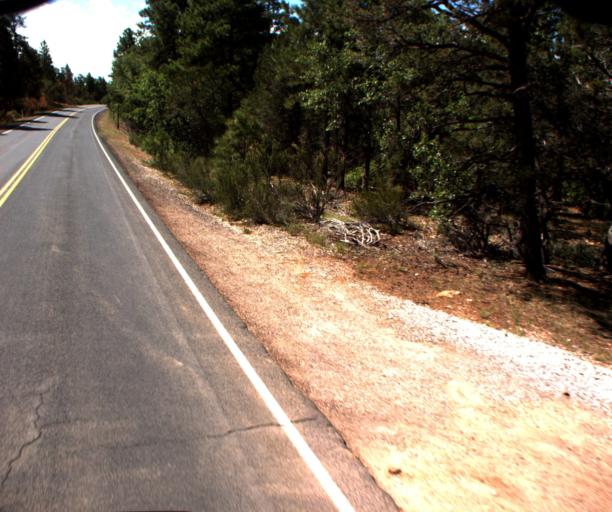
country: US
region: Arizona
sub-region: Coconino County
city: Grand Canyon
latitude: 36.0280
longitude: -112.0656
